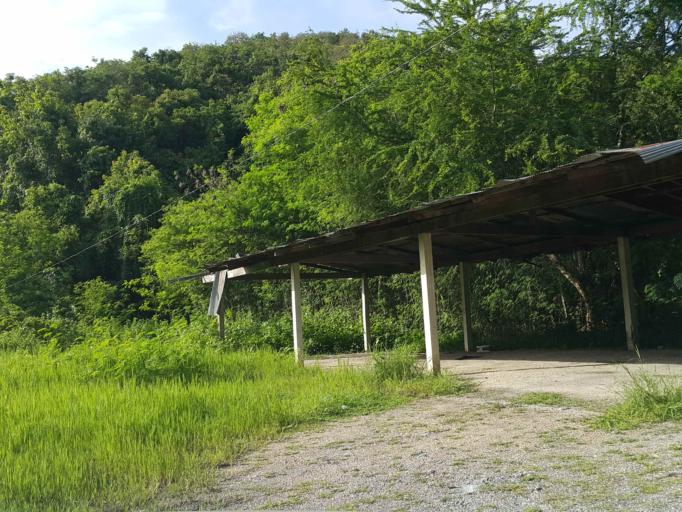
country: TH
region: Chiang Mai
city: San Sai
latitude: 18.9387
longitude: 99.1420
